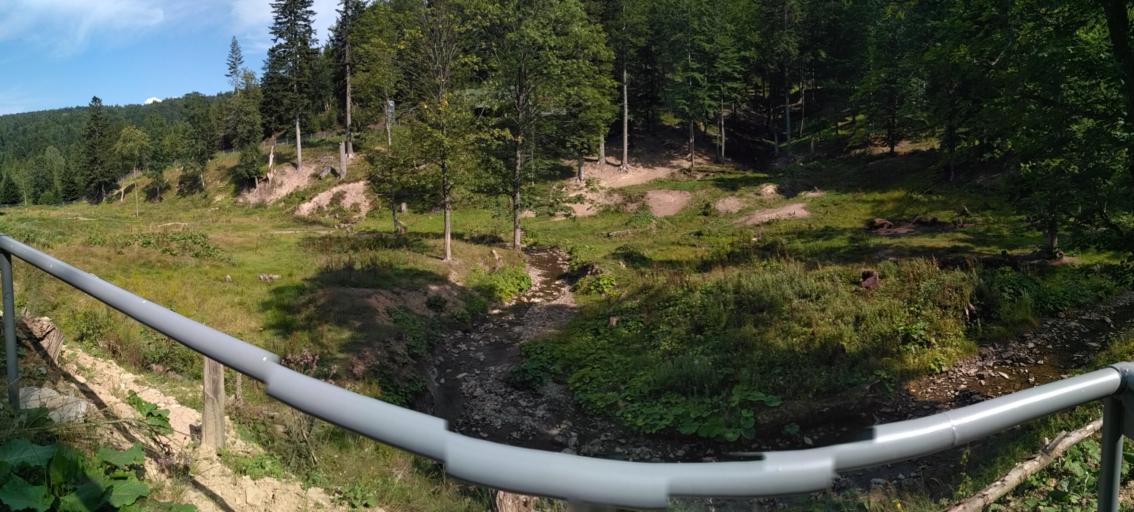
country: PL
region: Subcarpathian Voivodeship
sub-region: Powiat bieszczadzki
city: Lutowiska
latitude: 49.1411
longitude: 22.7123
